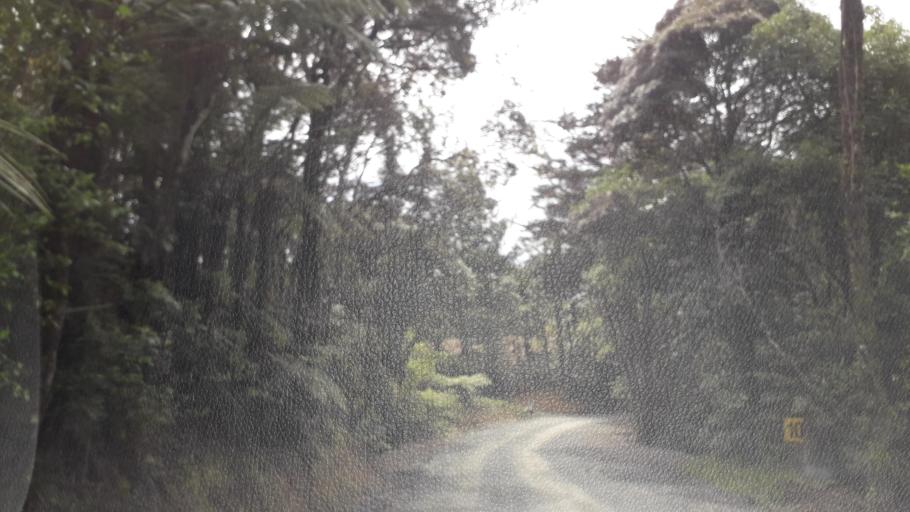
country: NZ
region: Northland
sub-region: Far North District
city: Kaitaia
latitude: -35.1999
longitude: 173.2799
